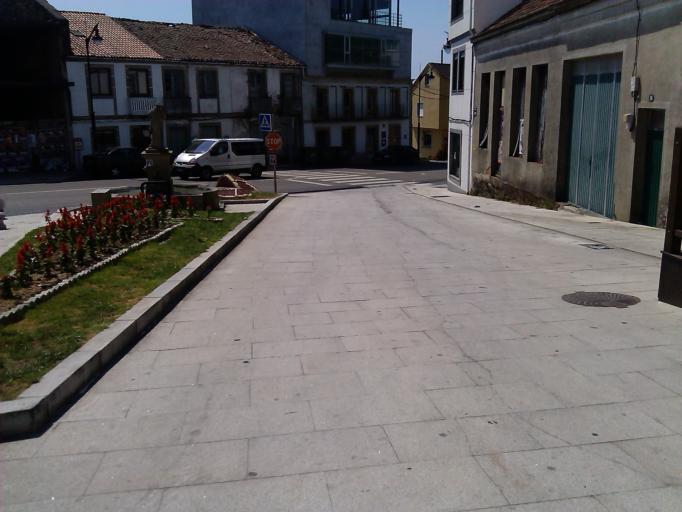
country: ES
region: Galicia
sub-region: Provincia de Lugo
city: Monterroso
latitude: 42.8733
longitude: -7.8698
